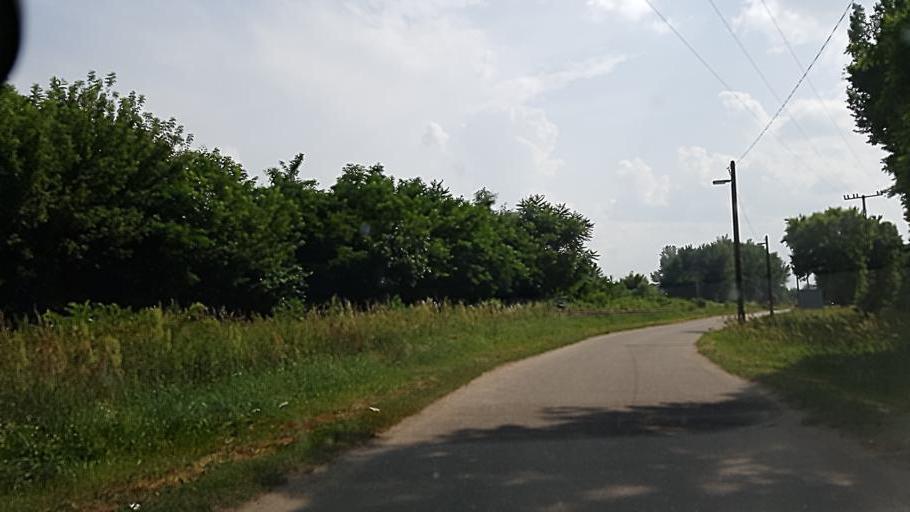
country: HU
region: Jasz-Nagykun-Szolnok
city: Tiszafured
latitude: 47.6235
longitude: 20.7443
